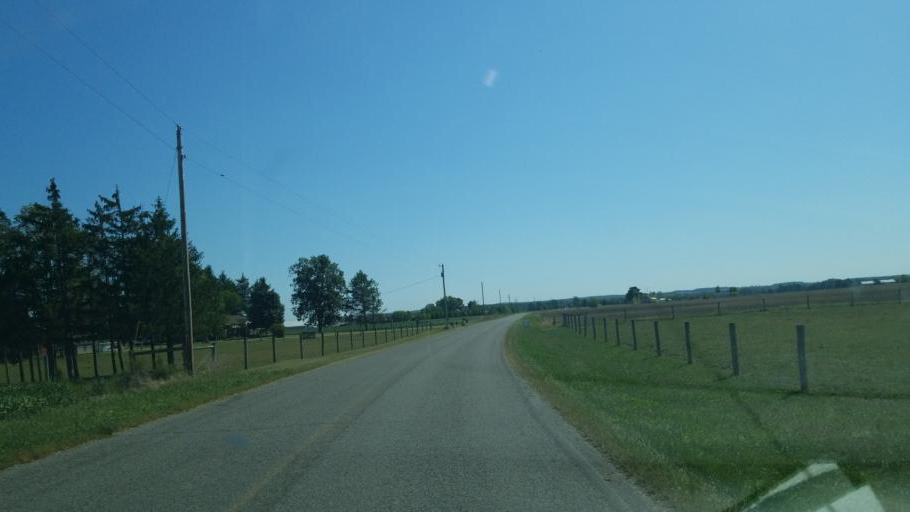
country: US
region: Ohio
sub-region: Logan County
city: Northwood
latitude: 40.5237
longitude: -83.7675
